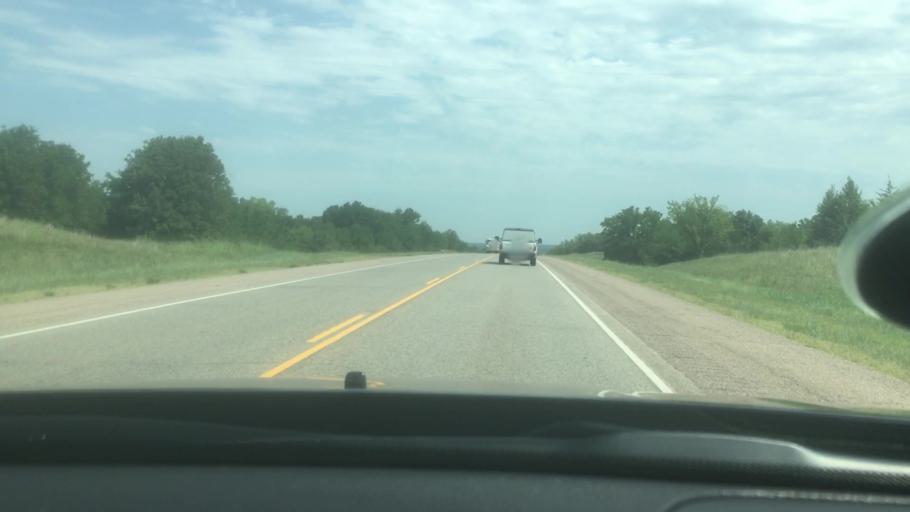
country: US
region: Oklahoma
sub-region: Seminole County
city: Maud
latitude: 35.0553
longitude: -96.9317
